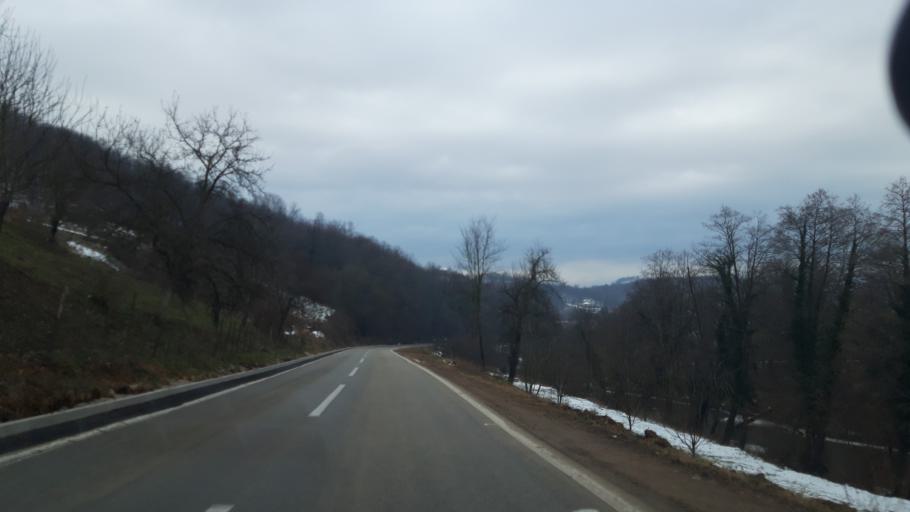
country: BA
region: Republika Srpska
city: Milici
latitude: 44.2319
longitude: 19.1045
